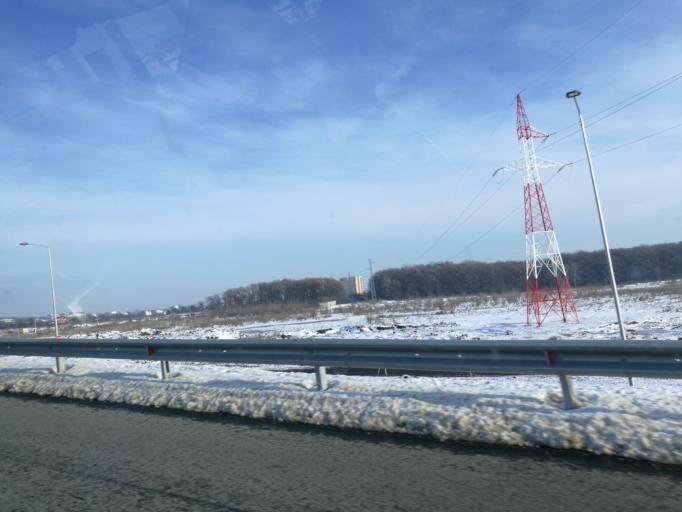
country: RO
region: Ilfov
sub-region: Voluntari City
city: Voluntari
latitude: 44.4908
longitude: 26.1478
